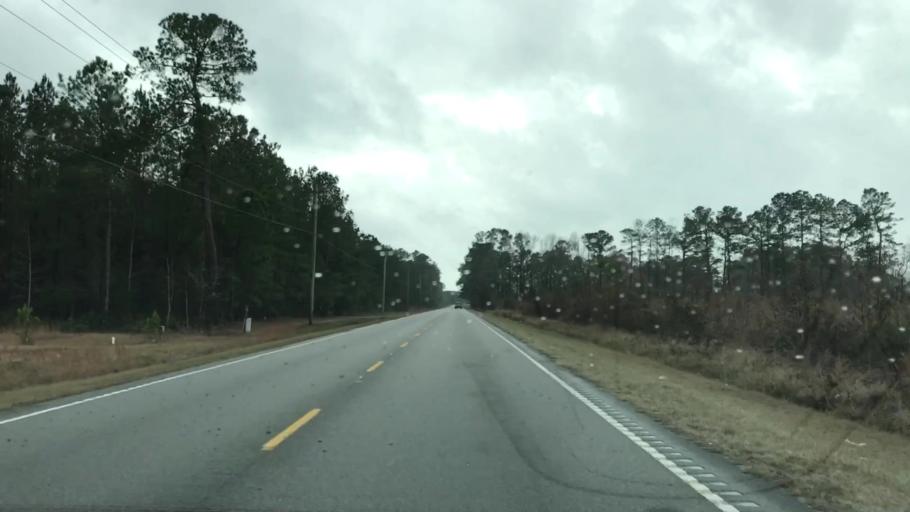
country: US
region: South Carolina
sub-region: Horry County
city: Socastee
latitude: 33.7328
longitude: -79.0829
